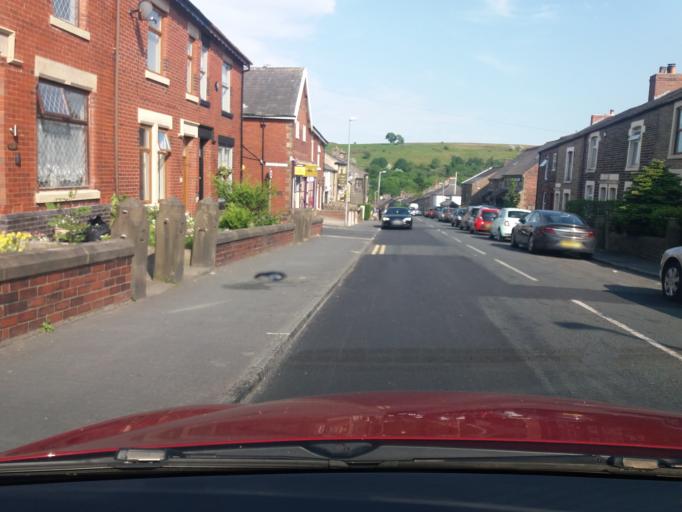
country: GB
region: England
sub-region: Lancashire
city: Chorley
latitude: 53.6885
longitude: -2.5703
